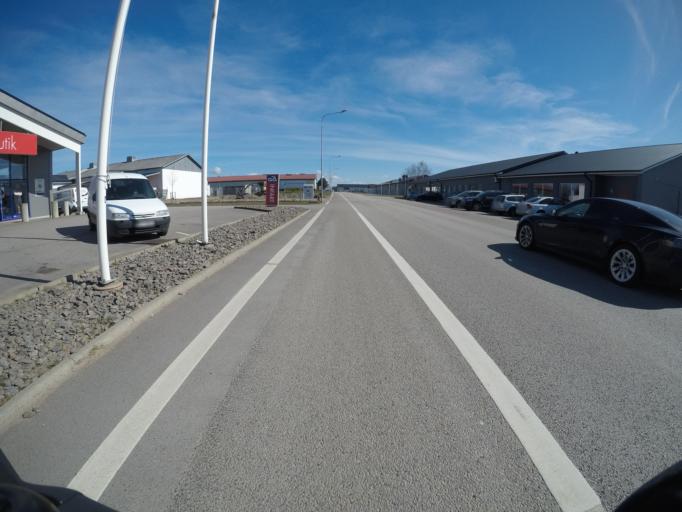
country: SE
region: Halland
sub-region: Laholms Kommun
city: Laholm
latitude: 56.5008
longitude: 13.0073
